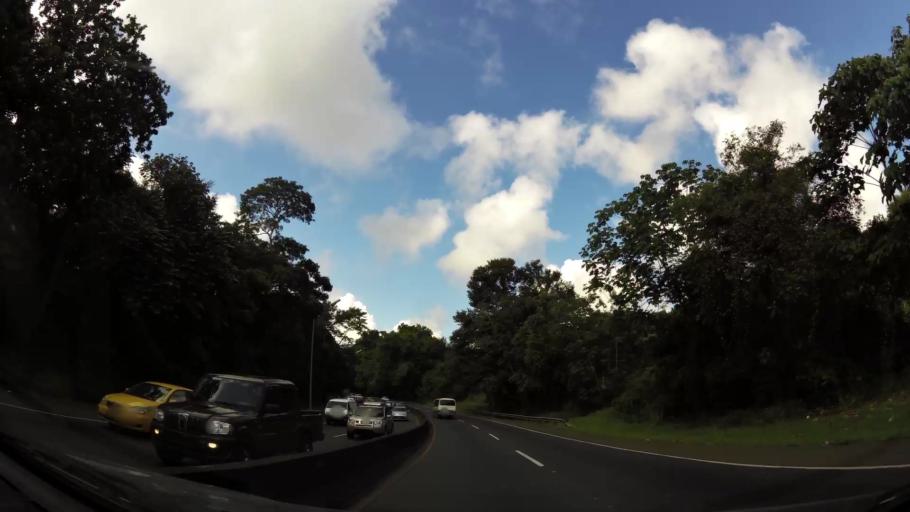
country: PA
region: Panama
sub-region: Distrito Arraijan
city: Arraijan
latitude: 8.9580
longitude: -79.6070
